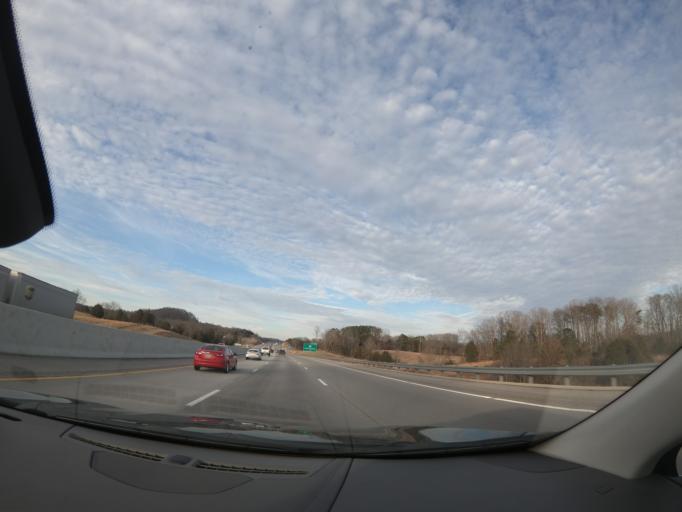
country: US
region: Kentucky
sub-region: Hart County
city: Munfordville
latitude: 37.2757
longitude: -85.9119
